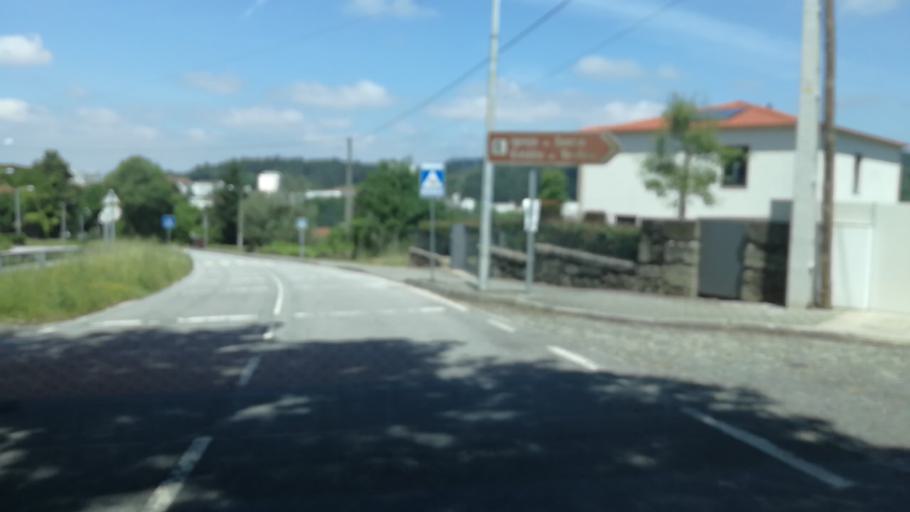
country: PT
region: Braga
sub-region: Braga
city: Adaufe
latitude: 41.5573
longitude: -8.3896
